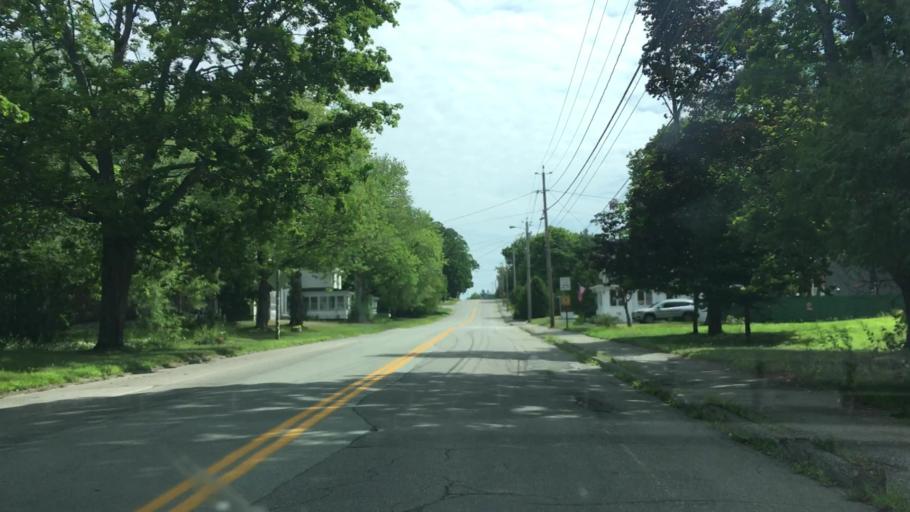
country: US
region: Maine
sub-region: Washington County
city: Calais
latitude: 45.1701
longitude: -67.2888
